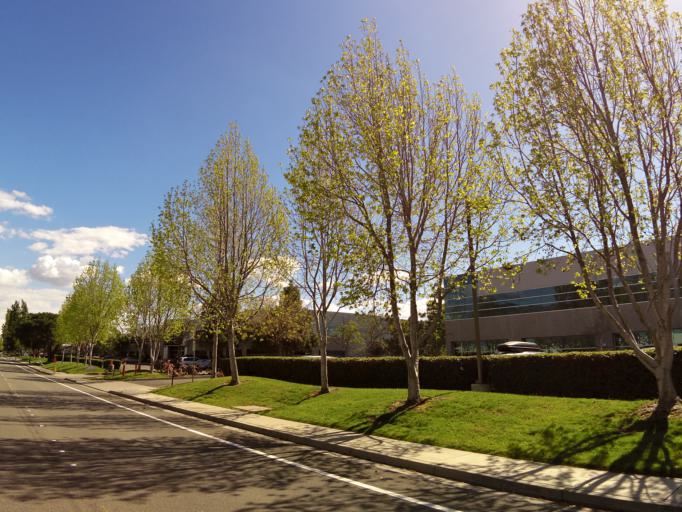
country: US
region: California
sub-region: Santa Clara County
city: Milpitas
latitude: 37.4688
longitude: -121.9363
